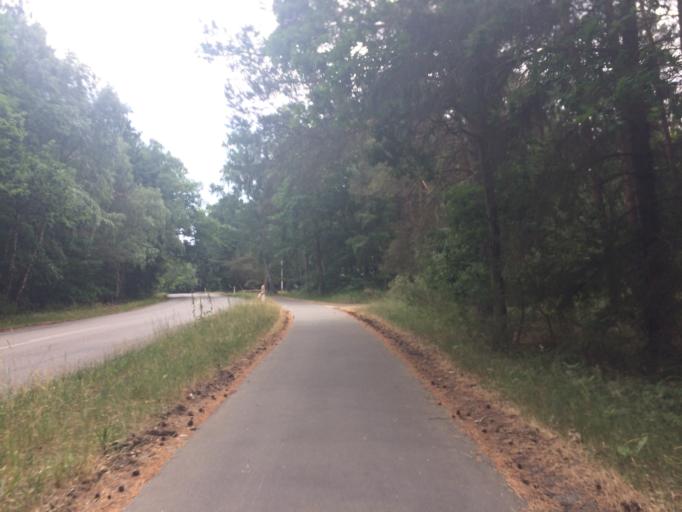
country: DK
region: Capital Region
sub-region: Bornholm Kommune
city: Ronne
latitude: 55.1681
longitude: 14.7131
